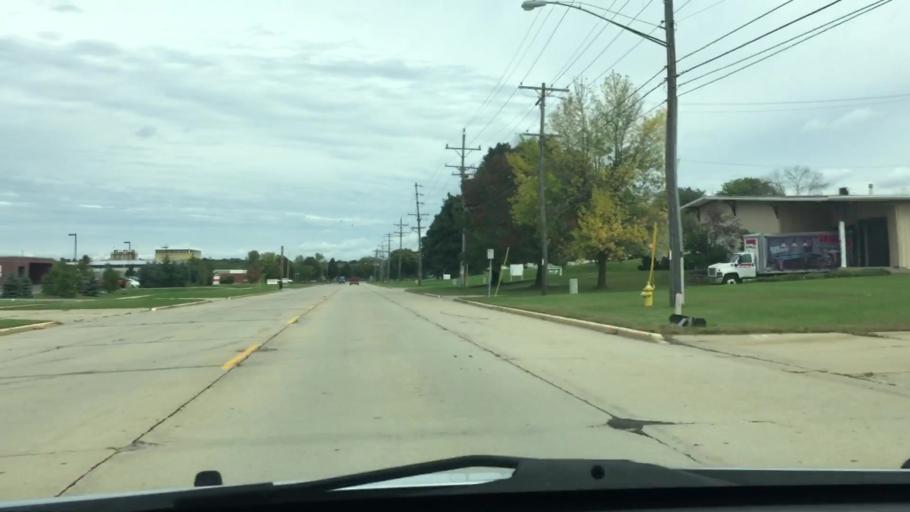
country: US
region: Wisconsin
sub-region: Waukesha County
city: Waukesha
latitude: 42.9903
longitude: -88.2498
